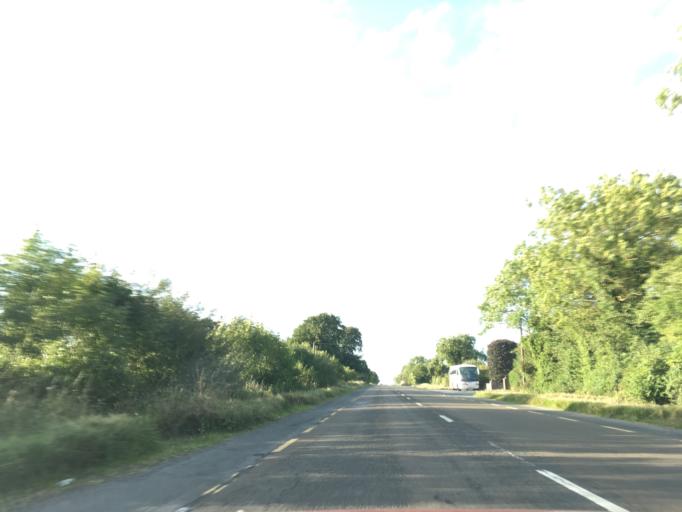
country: IE
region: Munster
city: Cashel
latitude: 52.4871
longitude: -7.8910
